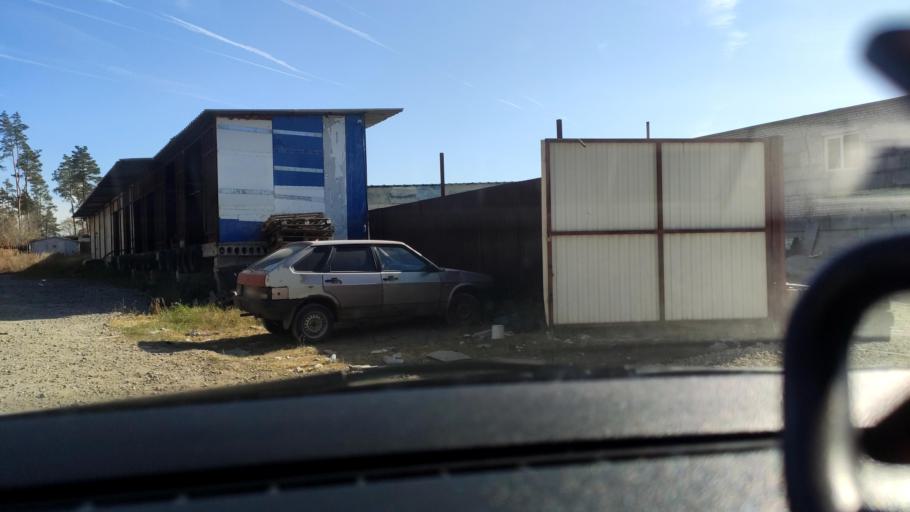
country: RU
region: Voronezj
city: Pridonskoy
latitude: 51.6417
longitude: 39.1142
